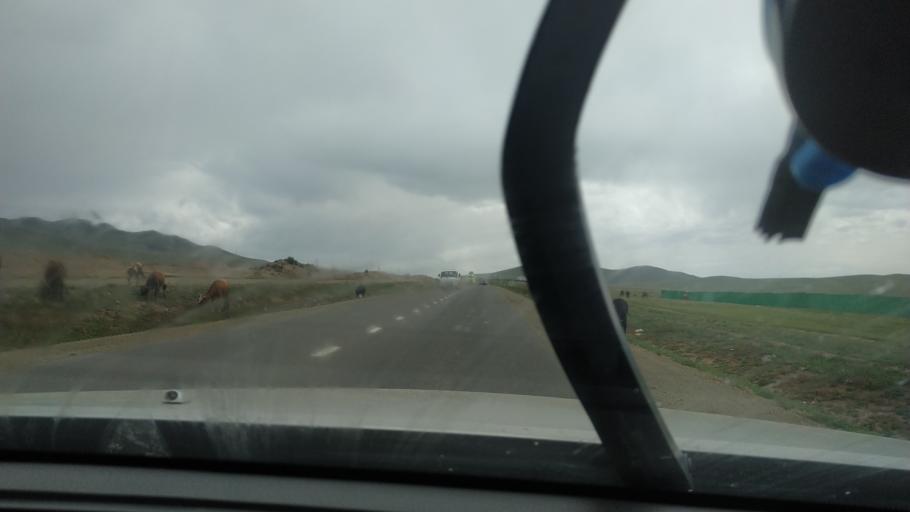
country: MN
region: Ulaanbaatar
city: Ulaanbaatar
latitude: 47.8128
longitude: 106.7539
